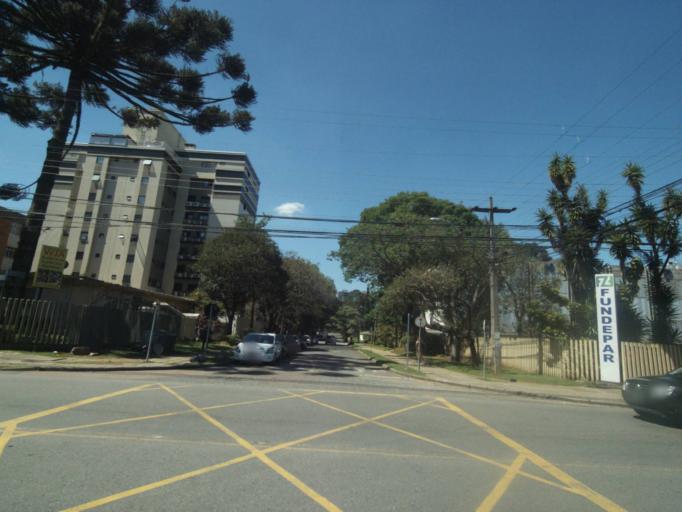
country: BR
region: Parana
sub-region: Curitiba
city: Curitiba
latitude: -25.4091
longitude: -49.2496
